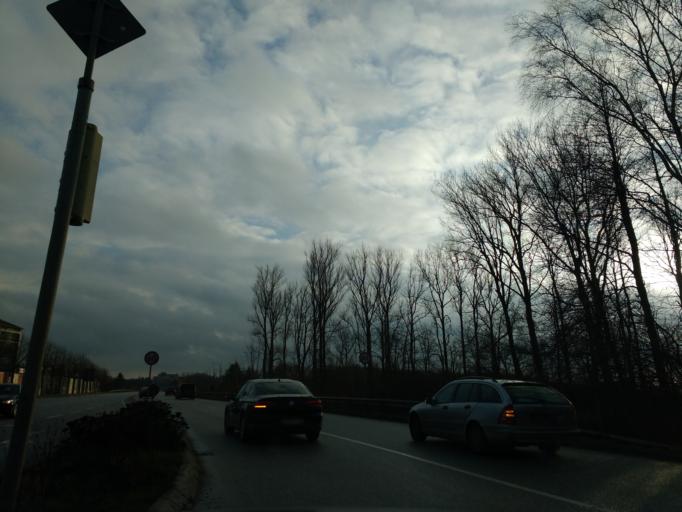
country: DE
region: Schleswig-Holstein
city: Windeby
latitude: 54.4722
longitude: 9.8261
